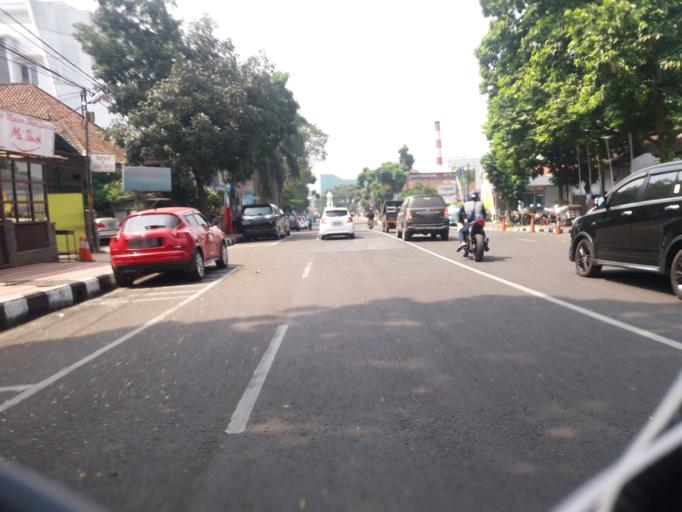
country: ID
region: West Java
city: Bandung
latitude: -6.9071
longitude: 107.6027
